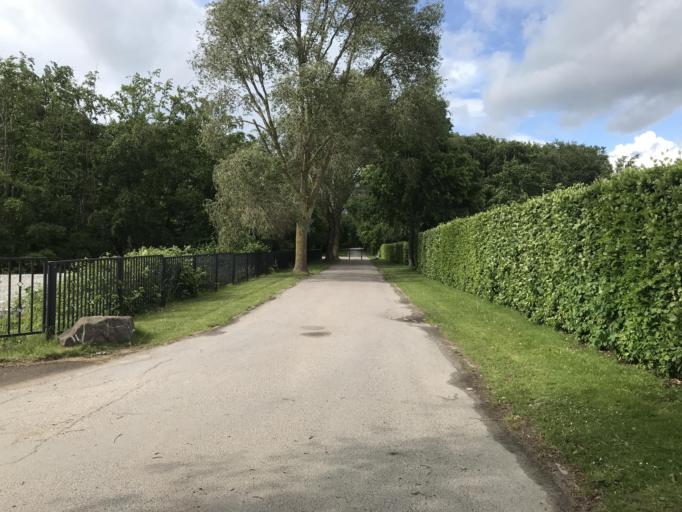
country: SE
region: Skane
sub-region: Burlovs Kommun
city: Arloev
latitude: 55.5920
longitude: 13.0507
